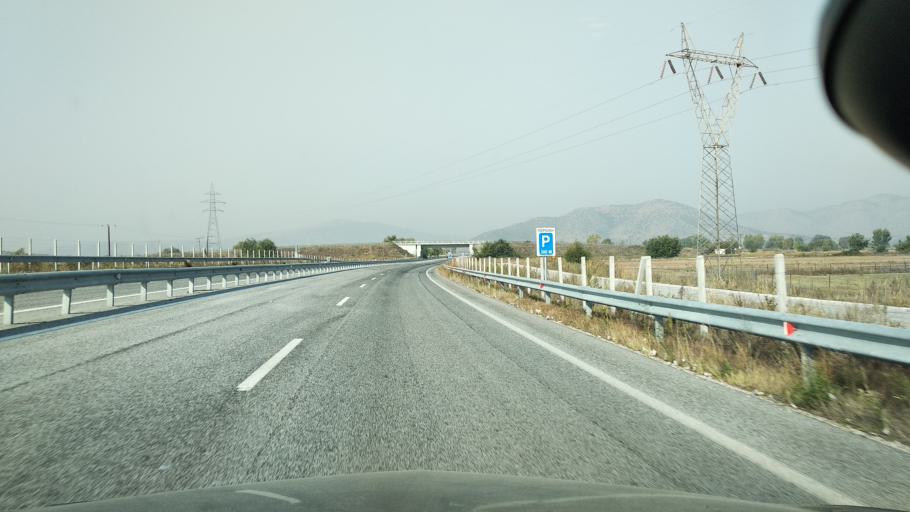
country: GR
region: Thessaly
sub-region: Trikala
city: Farkadona
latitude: 39.5831
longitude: 22.0519
